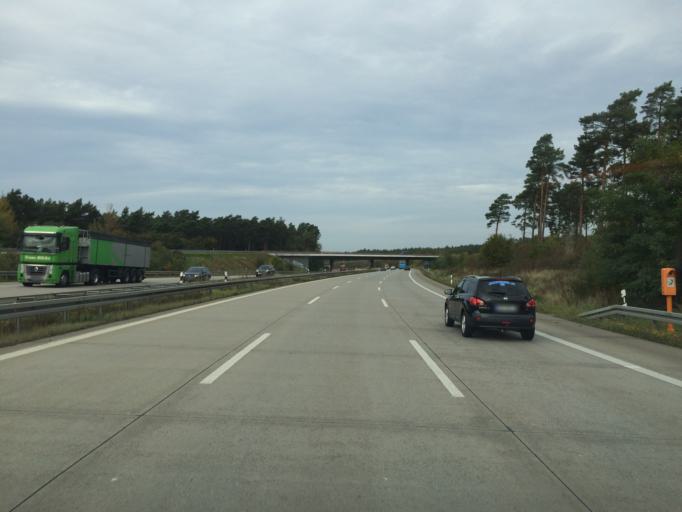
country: DE
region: Brandenburg
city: Gross Kreutz
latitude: 52.3323
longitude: 12.8173
